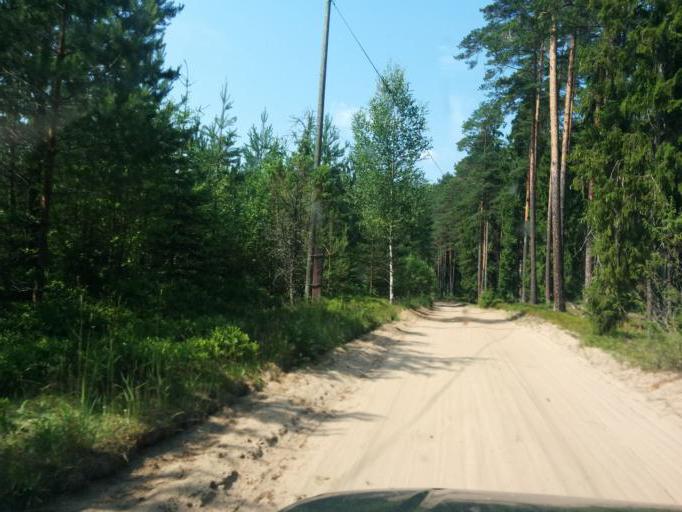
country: LV
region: Ikskile
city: Ikskile
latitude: 56.7446
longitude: 24.4894
